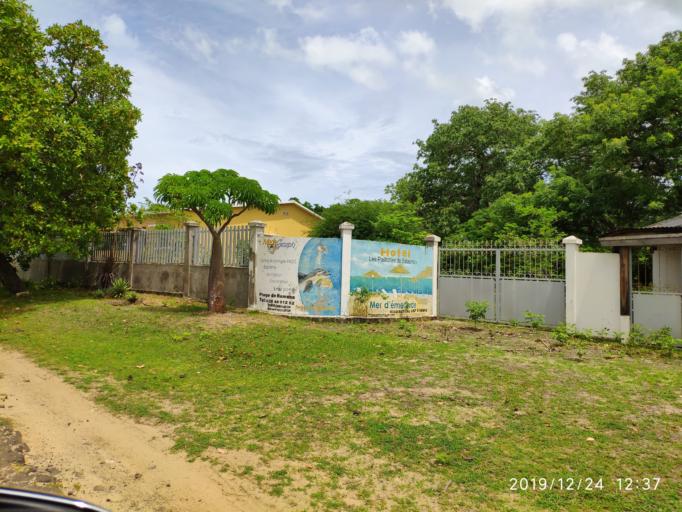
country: MG
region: Diana
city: Antsiranana
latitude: -12.3032
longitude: 49.3543
